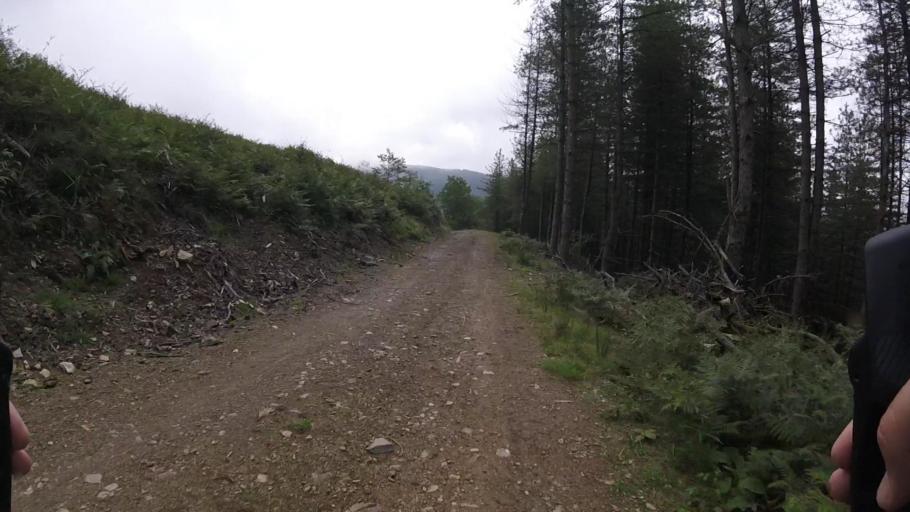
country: ES
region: Navarre
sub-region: Provincia de Navarra
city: Arano
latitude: 43.2522
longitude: -1.8756
